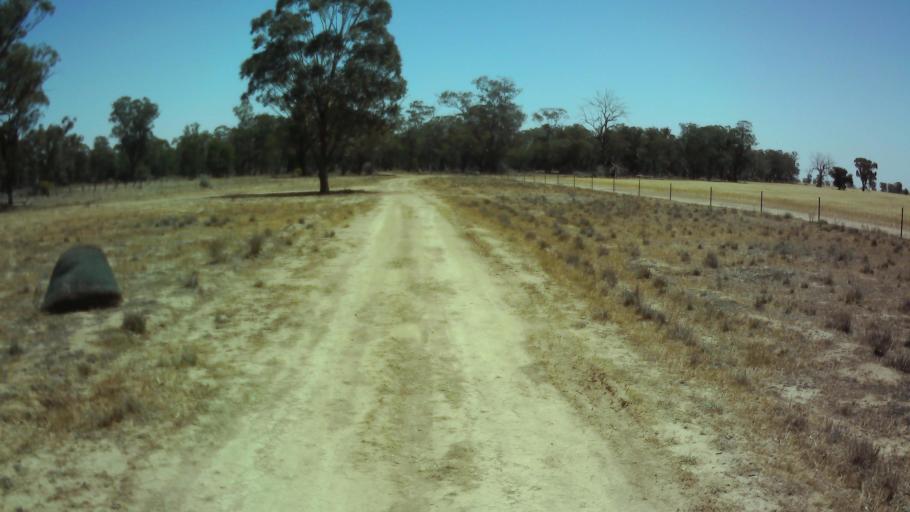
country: AU
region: New South Wales
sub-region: Weddin
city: Grenfell
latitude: -34.0695
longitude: 147.7927
